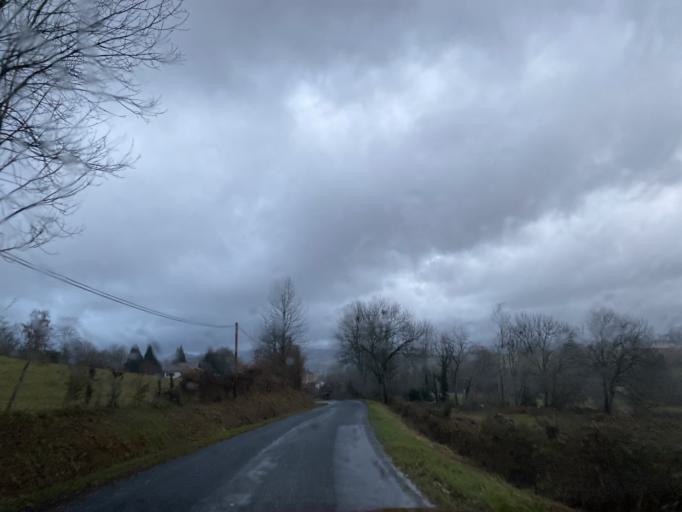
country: FR
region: Auvergne
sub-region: Departement du Puy-de-Dome
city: La Monnerie-le-Montel
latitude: 45.8510
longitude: 3.6091
